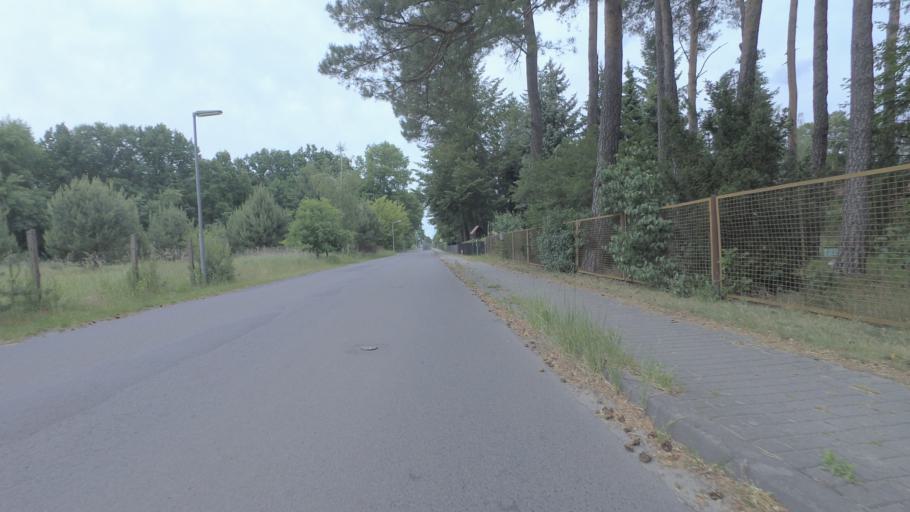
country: DE
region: Brandenburg
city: Bestensee
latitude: 52.2733
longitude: 13.7428
